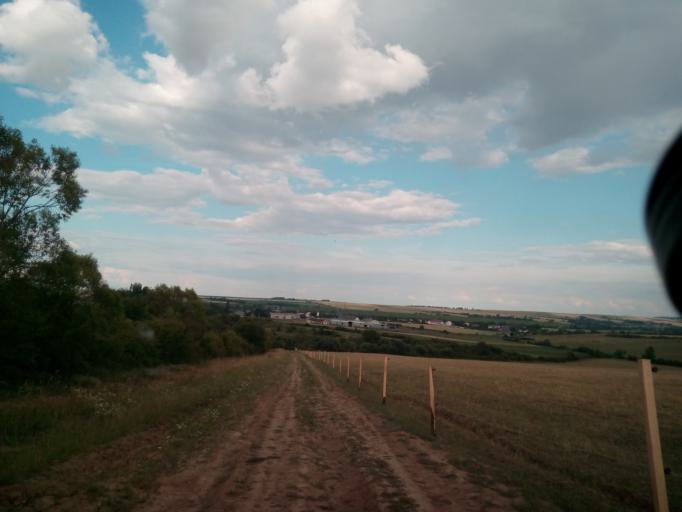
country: SK
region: Kosicky
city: Secovce
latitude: 48.5789
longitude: 21.5472
